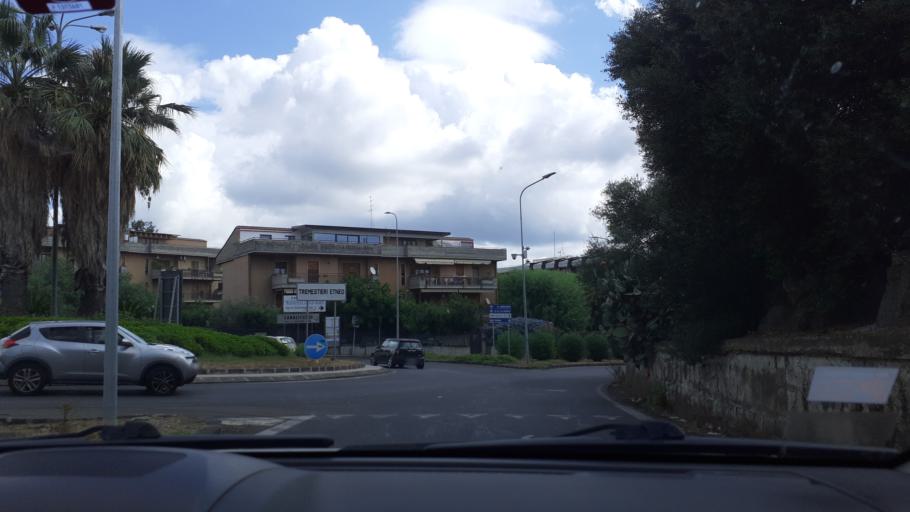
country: IT
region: Sicily
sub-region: Catania
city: Canalicchio
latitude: 37.5390
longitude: 15.0944
